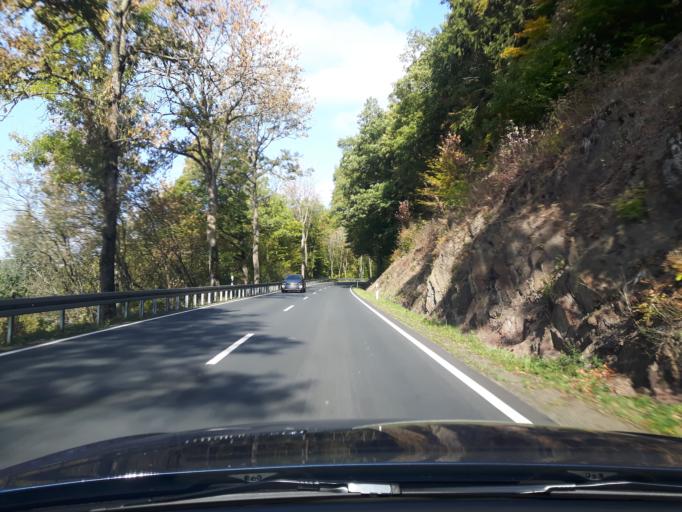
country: DE
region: Hesse
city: Hatzfeld
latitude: 50.9680
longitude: 8.5869
